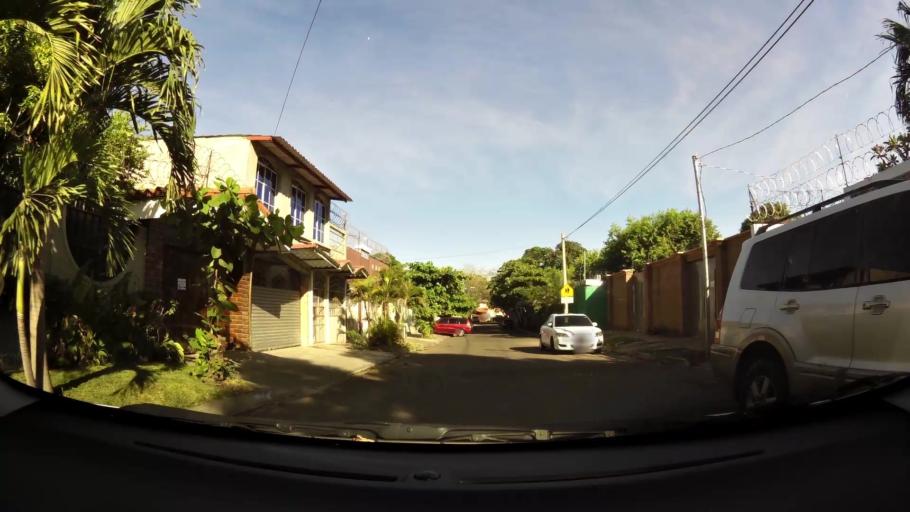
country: SV
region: San Miguel
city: San Miguel
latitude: 13.4731
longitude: -88.1869
